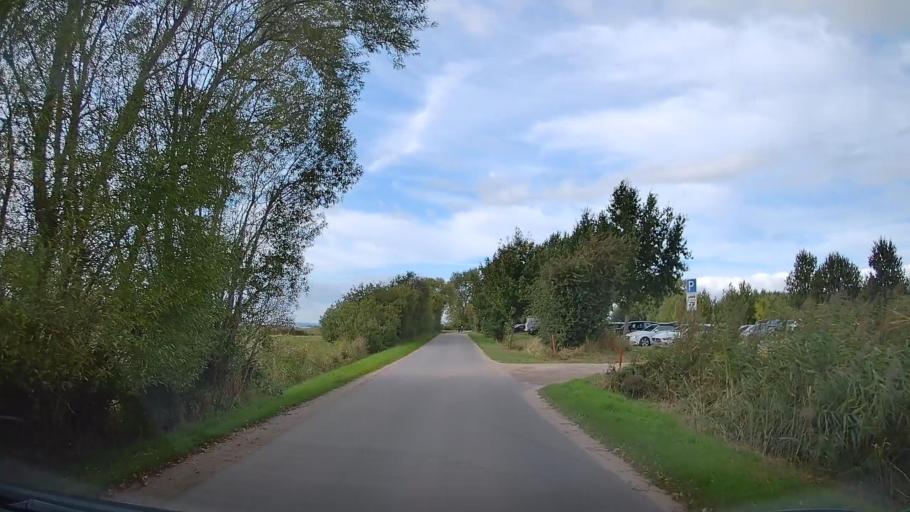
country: DE
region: Schleswig-Holstein
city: Gelting
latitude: 54.7682
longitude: 9.9086
